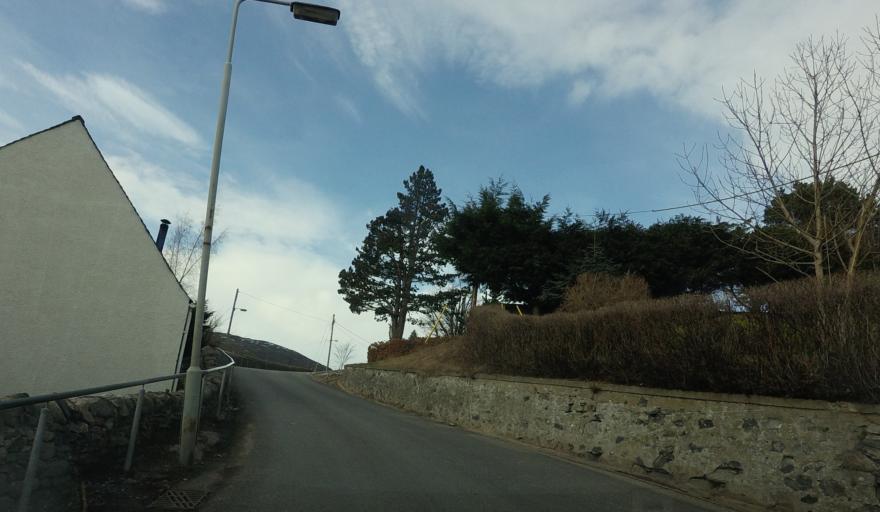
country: GB
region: Scotland
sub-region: Highland
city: Kingussie
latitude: 57.0807
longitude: -4.0516
